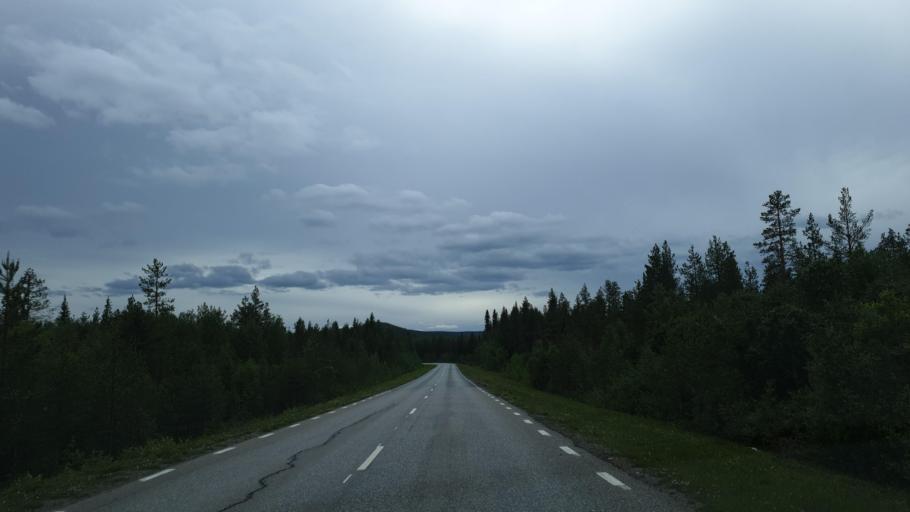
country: SE
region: Vaesterbotten
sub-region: Sorsele Kommun
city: Sorsele
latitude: 65.5305
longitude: 17.3924
